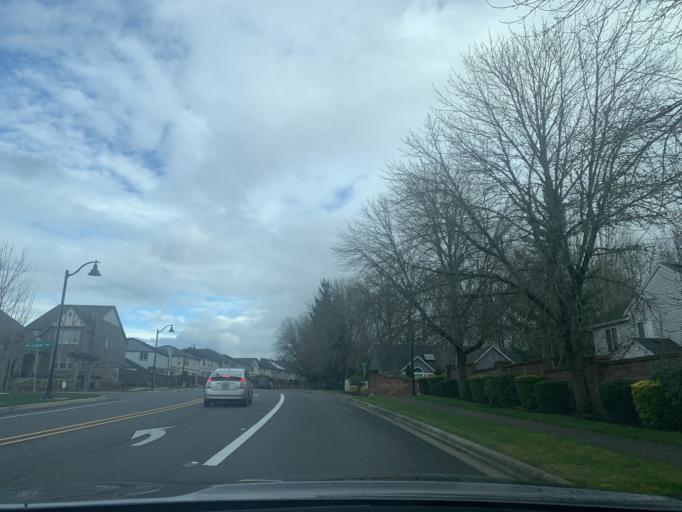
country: US
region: Oregon
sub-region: Washington County
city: Oak Hills
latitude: 45.5674
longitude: -122.8309
